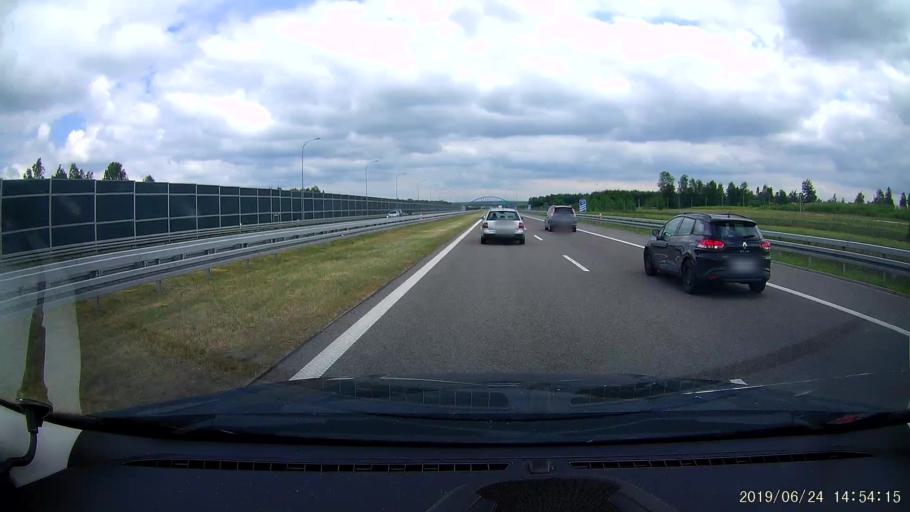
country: PL
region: Subcarpathian Voivodeship
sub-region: Powiat ropczycko-sedziszowski
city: Sedziszow Malopolski
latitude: 50.1093
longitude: 21.6543
